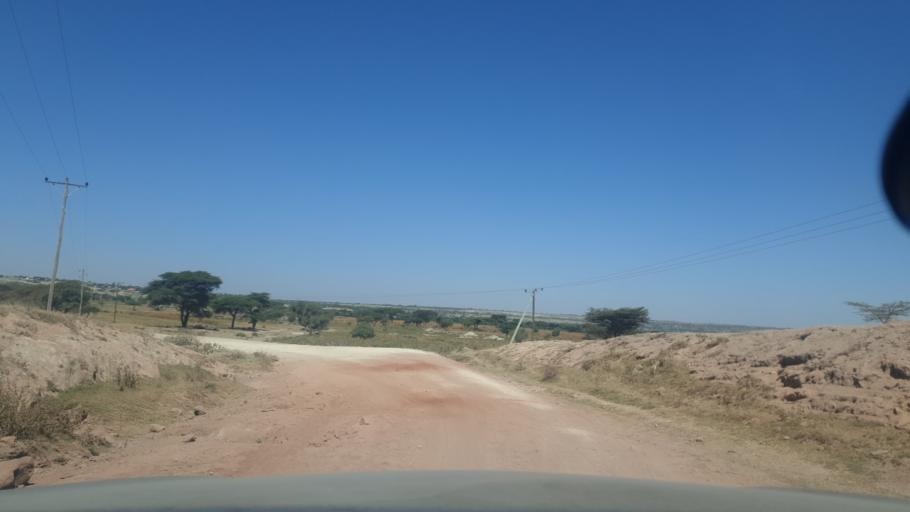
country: ET
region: Oromiya
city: Shashemene
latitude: 7.5073
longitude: 38.6881
